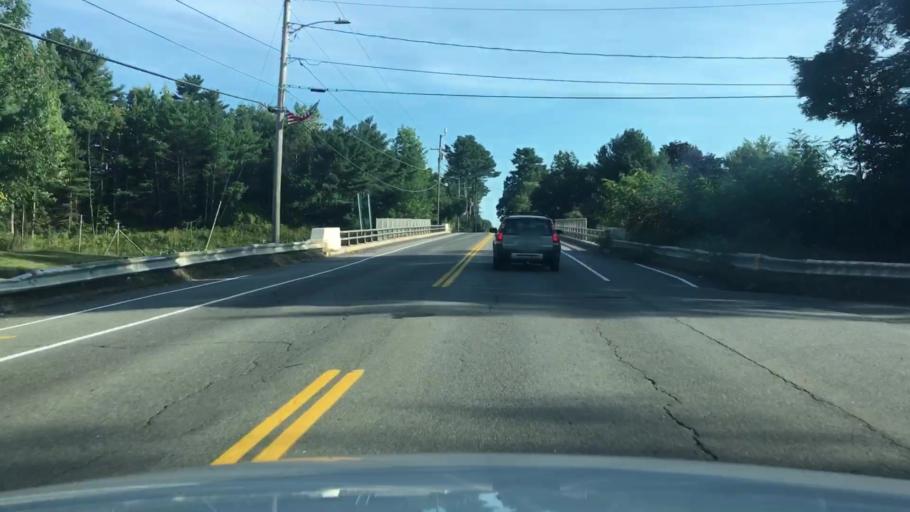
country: US
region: Maine
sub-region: Cumberland County
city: Falmouth
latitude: 43.7256
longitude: -70.2946
